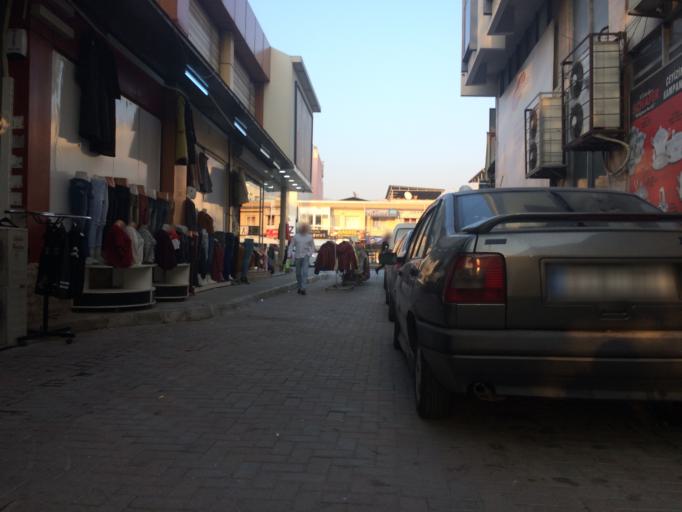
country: TR
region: Izmir
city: Karsiyaka
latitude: 38.4926
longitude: 27.0634
